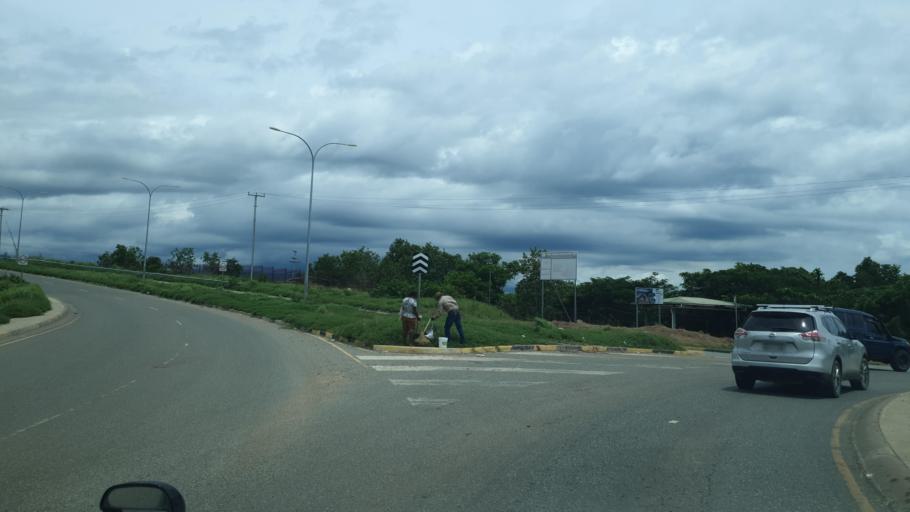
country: PG
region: National Capital
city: Port Moresby
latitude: -9.5003
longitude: 147.2346
